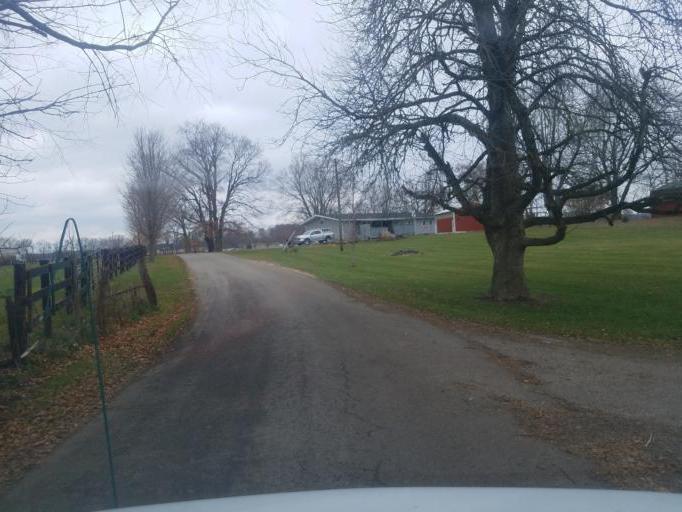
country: US
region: Ohio
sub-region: Knox County
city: Fredericktown
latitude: 40.5001
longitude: -82.5274
